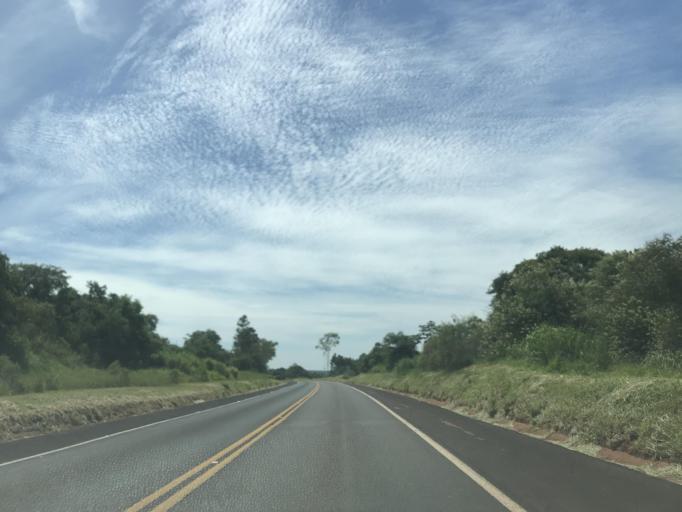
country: BR
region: Parana
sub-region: Paranavai
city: Nova Aurora
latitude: -22.9594
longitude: -52.6882
